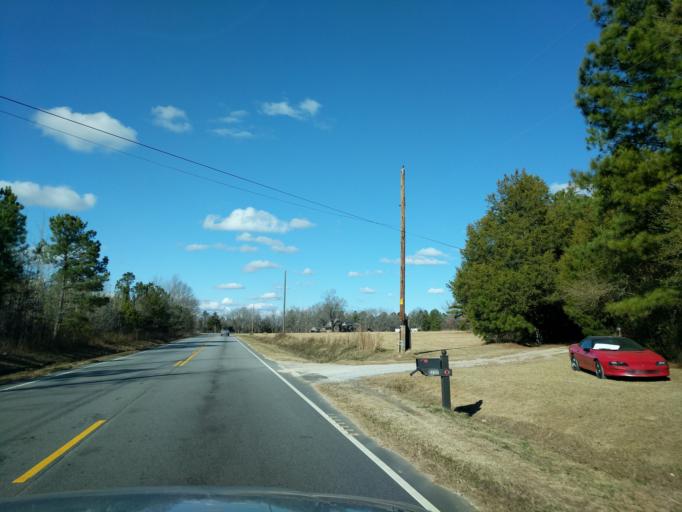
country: US
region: South Carolina
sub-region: Greenwood County
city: Ninety Six
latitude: 34.1037
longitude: -82.1036
